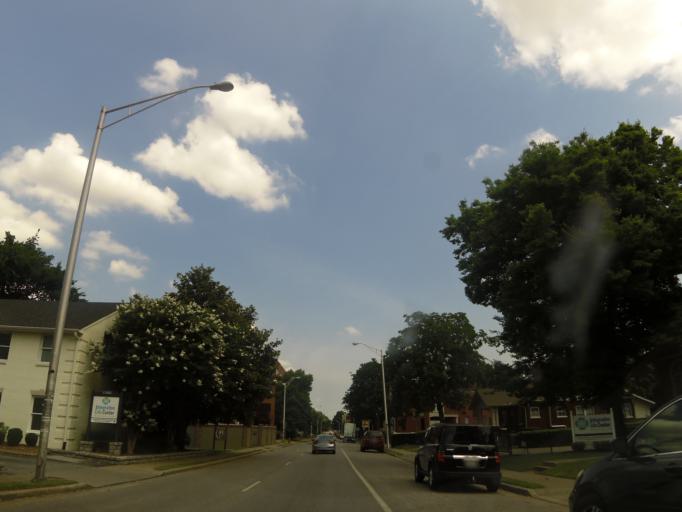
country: US
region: Tennessee
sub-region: Davidson County
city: Nashville
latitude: 36.1438
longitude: -86.7931
